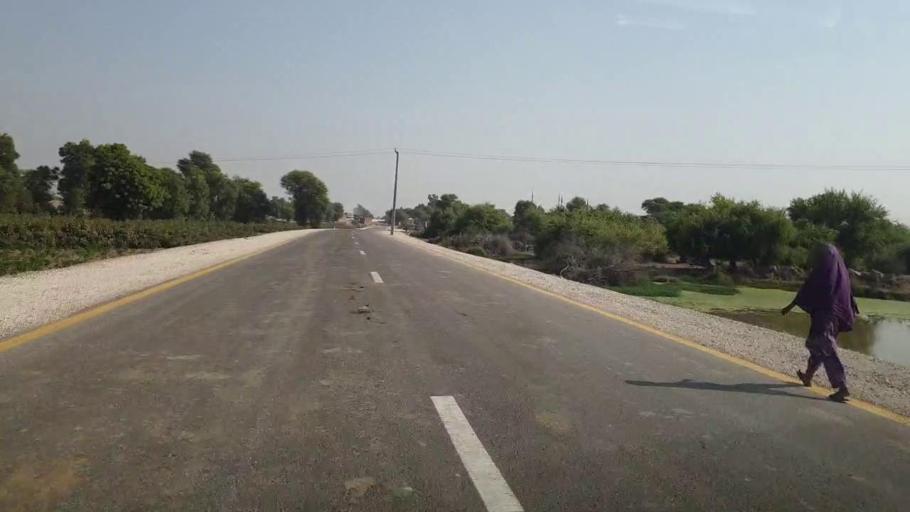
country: PK
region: Sindh
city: Bhan
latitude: 26.5648
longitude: 67.7710
